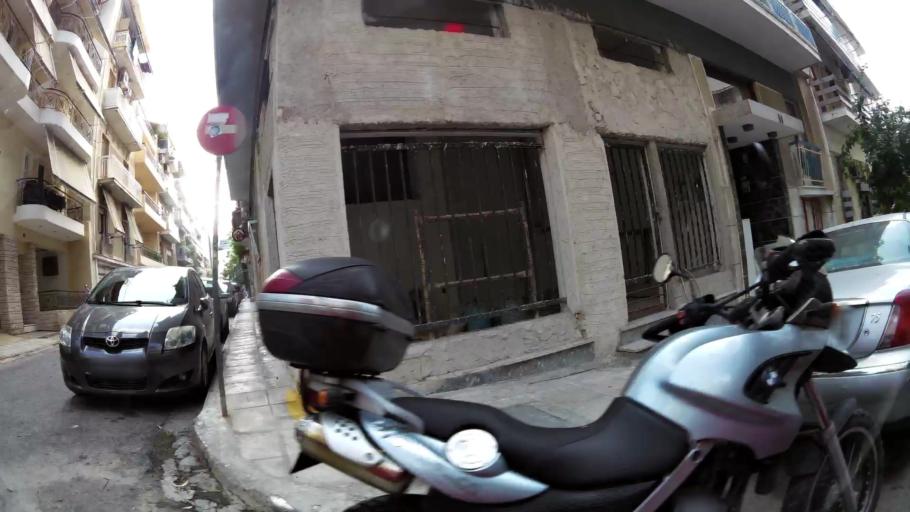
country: GR
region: Attica
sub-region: Nomarchia Athinas
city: Dhafni
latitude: 37.9591
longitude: 23.7303
